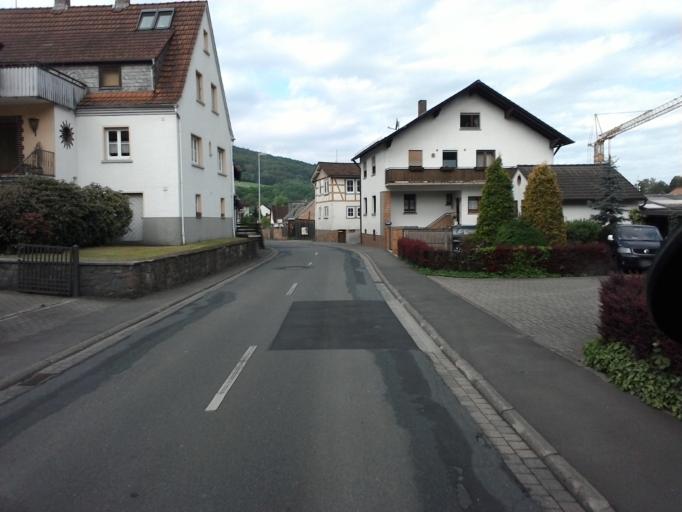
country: DE
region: Bavaria
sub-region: Regierungsbezirk Unterfranken
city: Waldaschaff
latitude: 49.9737
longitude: 9.3090
